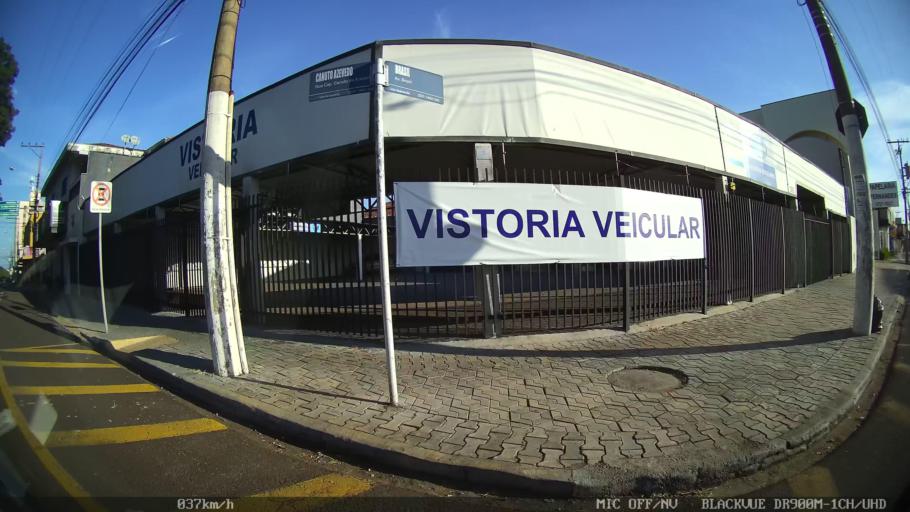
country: BR
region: Sao Paulo
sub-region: Franca
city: Franca
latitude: -20.5273
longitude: -47.3902
